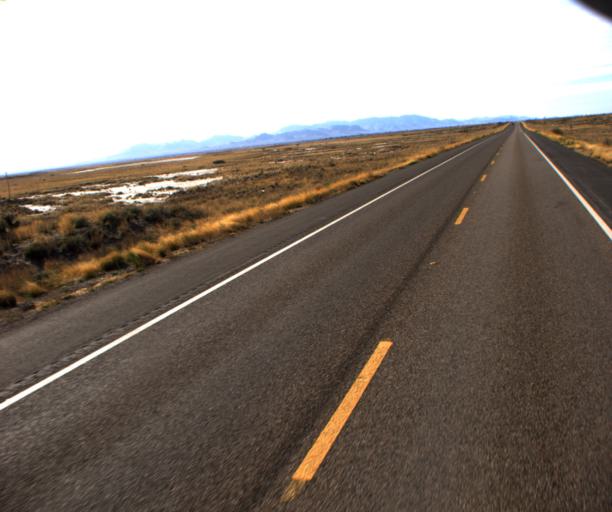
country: US
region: Arizona
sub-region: Cochise County
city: Willcox
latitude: 32.2129
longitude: -109.7806
